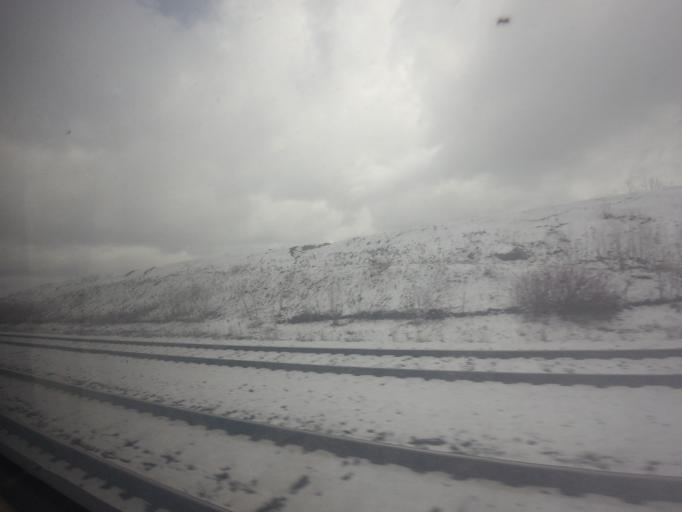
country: CA
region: Ontario
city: Scarborough
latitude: 43.7242
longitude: -79.2502
